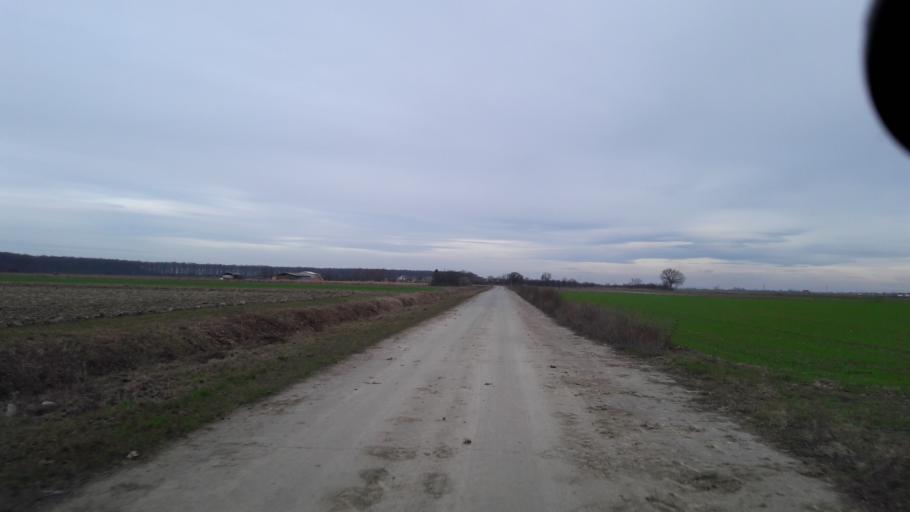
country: HR
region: Osjecko-Baranjska
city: Vladislavci
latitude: 45.4403
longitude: 18.5669
